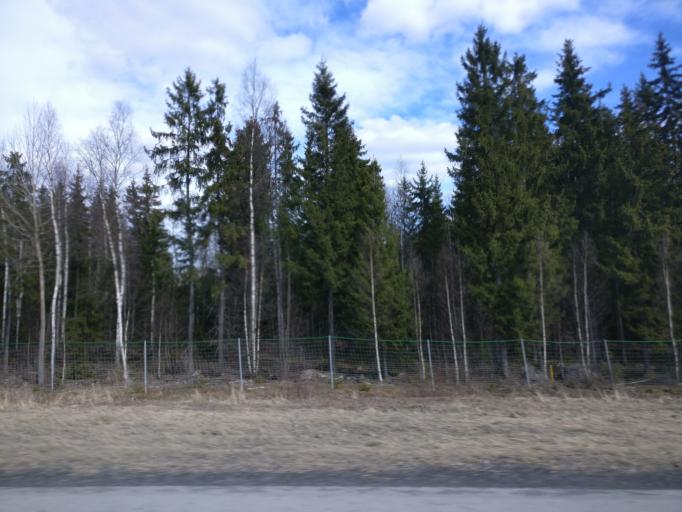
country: FI
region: Pirkanmaa
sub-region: Tampere
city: Lempaeaelae
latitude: 61.2732
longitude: 23.8151
